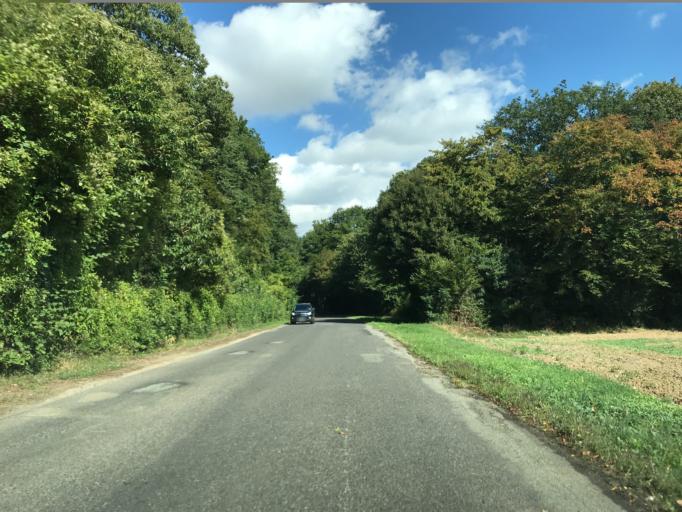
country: FR
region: Haute-Normandie
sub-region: Departement de l'Eure
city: La Chapelle-Reanville
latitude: 49.0818
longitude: 1.3953
